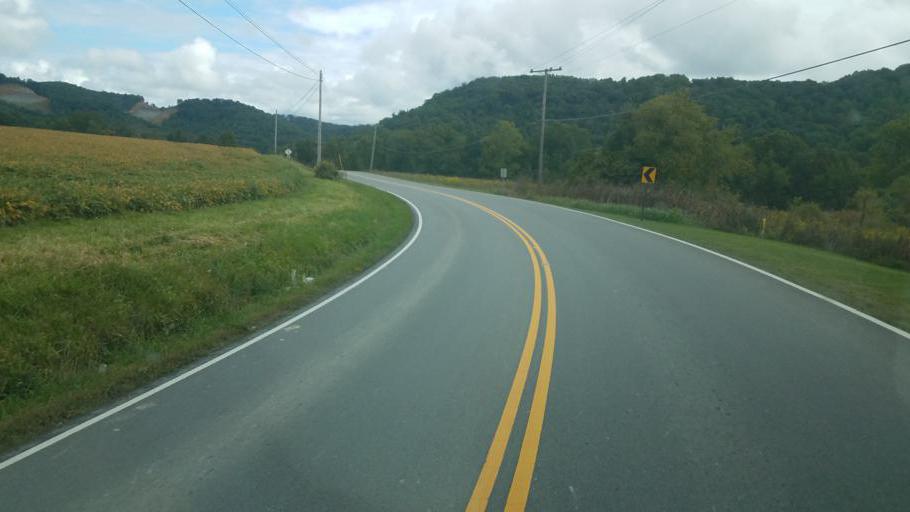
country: US
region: Ohio
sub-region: Scioto County
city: Lucasville
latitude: 38.8719
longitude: -82.9585
